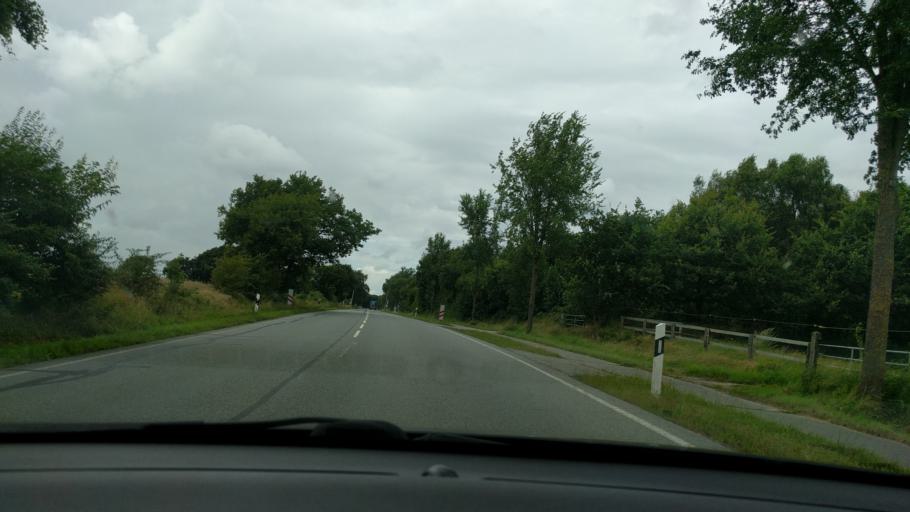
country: DE
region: Schleswig-Holstein
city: Weddingstedt
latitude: 54.2232
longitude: 9.0842
